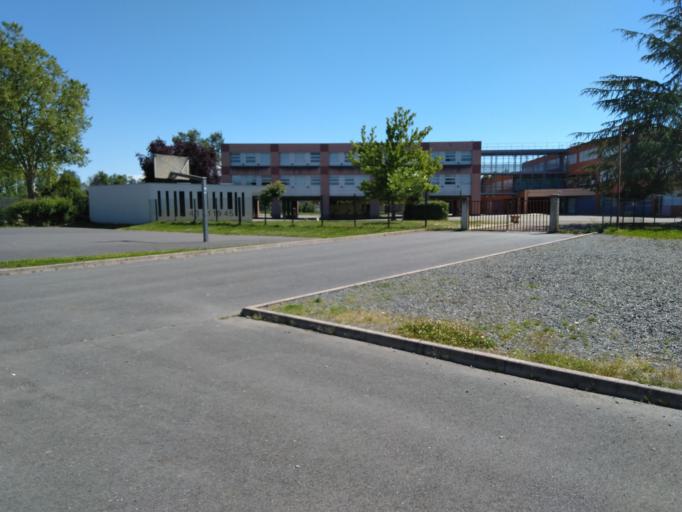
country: FR
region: Midi-Pyrenees
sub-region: Departement du Tarn
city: Lavaur
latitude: 43.6892
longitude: 1.8185
